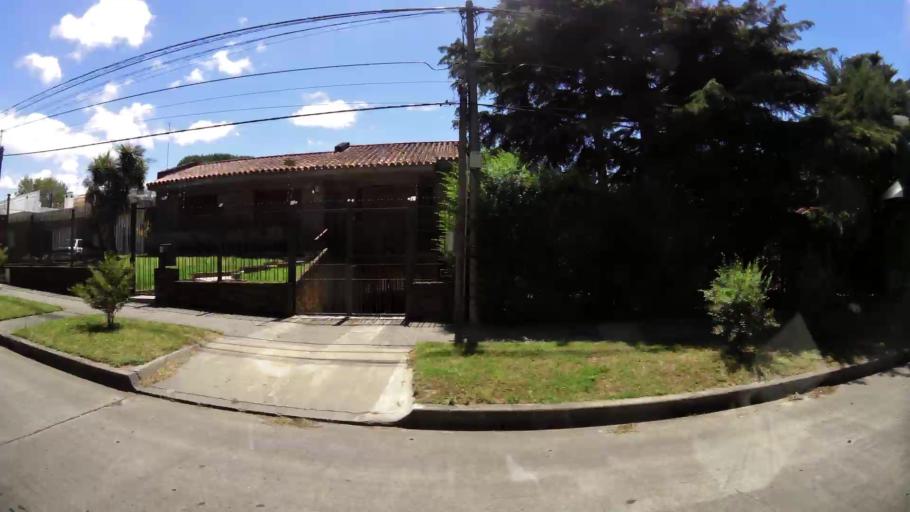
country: UY
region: Canelones
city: Paso de Carrasco
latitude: -34.8891
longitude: -56.0962
